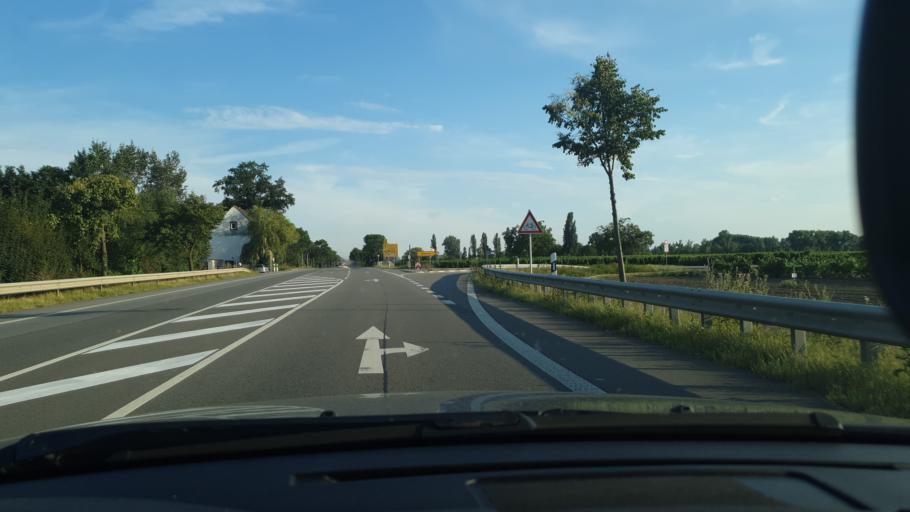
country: DE
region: Rheinland-Pfalz
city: Mettenheim
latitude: 49.7377
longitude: 8.3505
